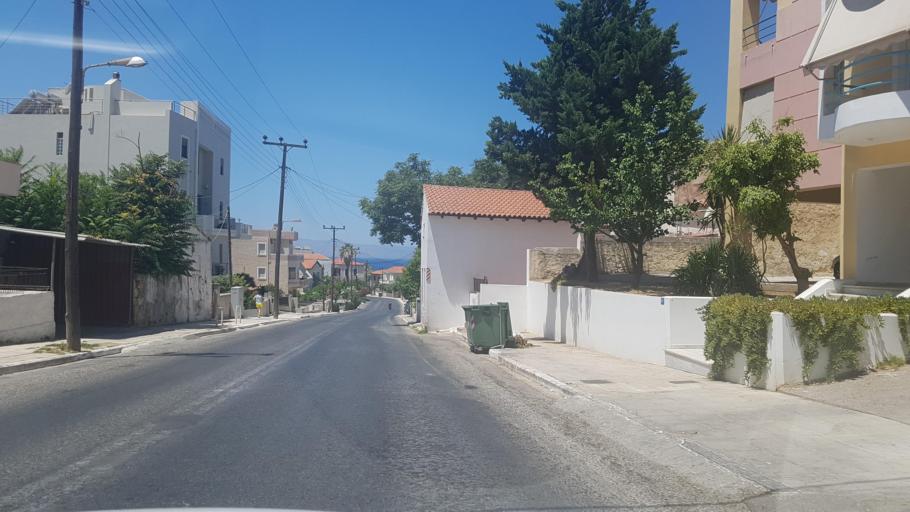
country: GR
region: Crete
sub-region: Nomos Chanias
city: Chania
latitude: 35.5159
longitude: 24.0355
